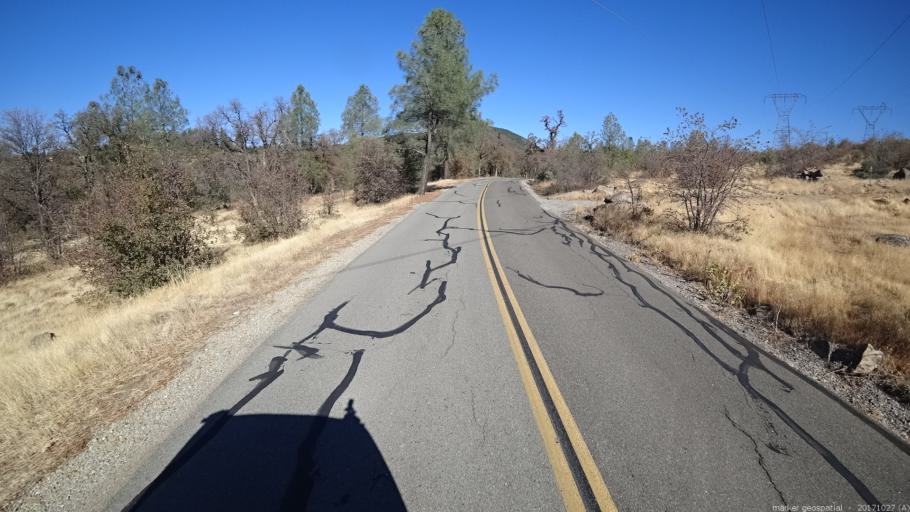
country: US
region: California
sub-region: Shasta County
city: Shingletown
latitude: 40.7776
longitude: -121.9594
